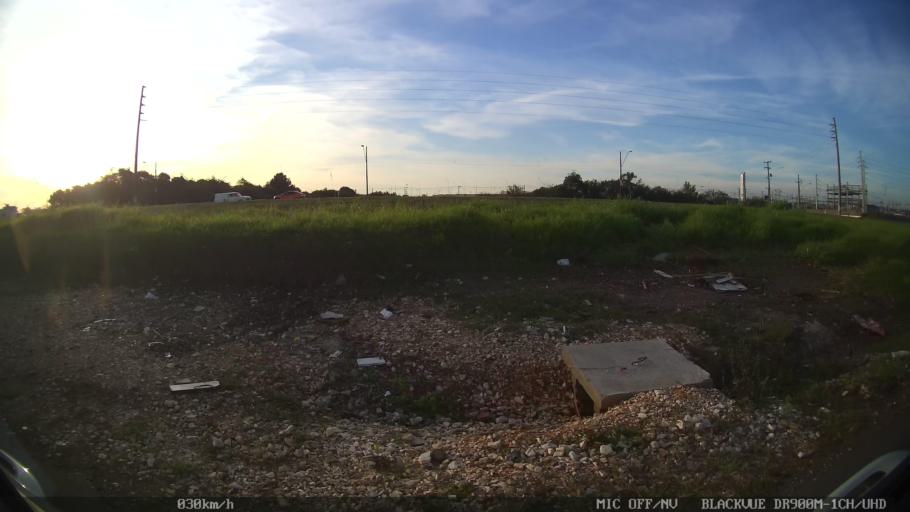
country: BR
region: Parana
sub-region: Pinhais
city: Pinhais
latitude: -25.4389
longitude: -49.1677
